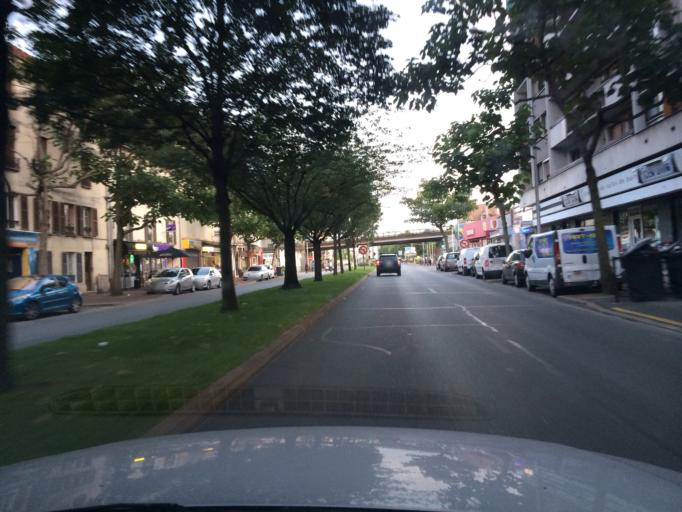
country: FR
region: Ile-de-France
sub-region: Departement du Val-de-Marne
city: Joinville-le-Pont
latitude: 48.8080
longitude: 2.4711
